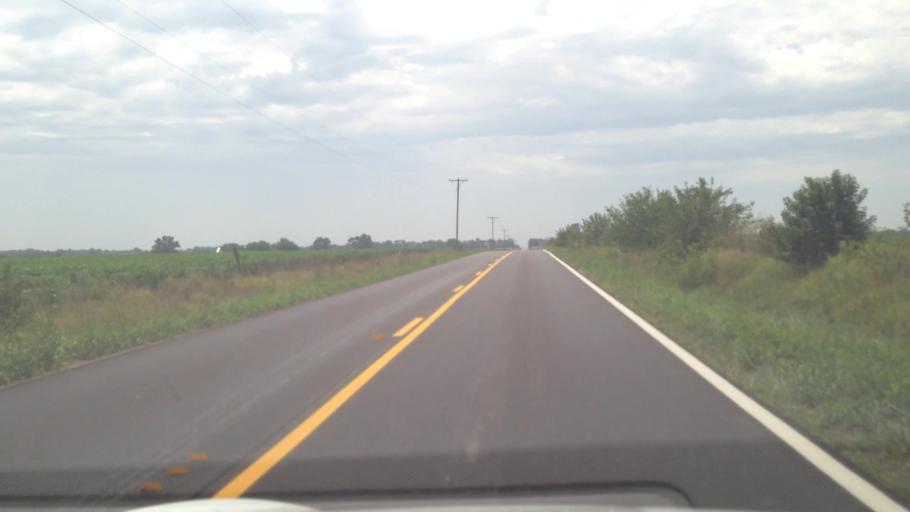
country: US
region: Kansas
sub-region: Crawford County
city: Girard
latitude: 37.6492
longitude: -94.9698
